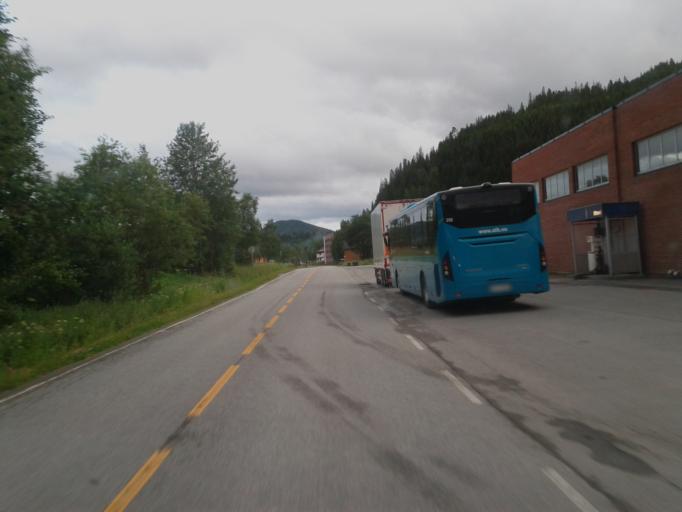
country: NO
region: Sor-Trondelag
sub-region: Midtre Gauldal
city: Storen
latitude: 63.0544
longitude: 10.2851
